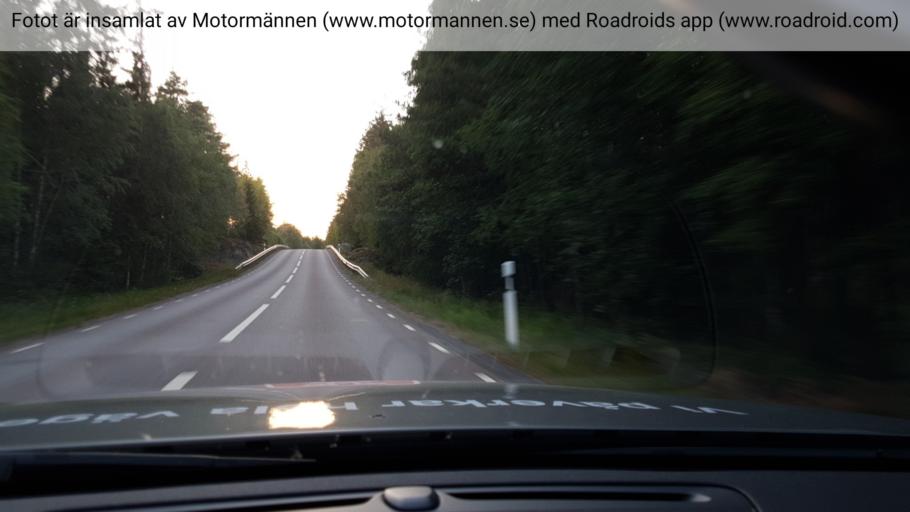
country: SE
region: Uppsala
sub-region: Heby Kommun
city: OEstervala
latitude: 60.0042
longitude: 17.3012
